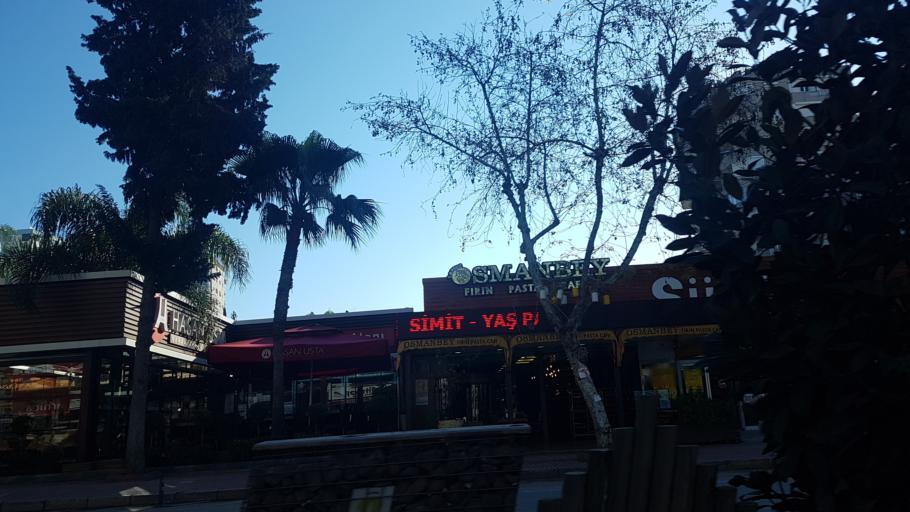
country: TR
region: Adana
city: Adana
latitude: 37.0203
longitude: 35.3161
